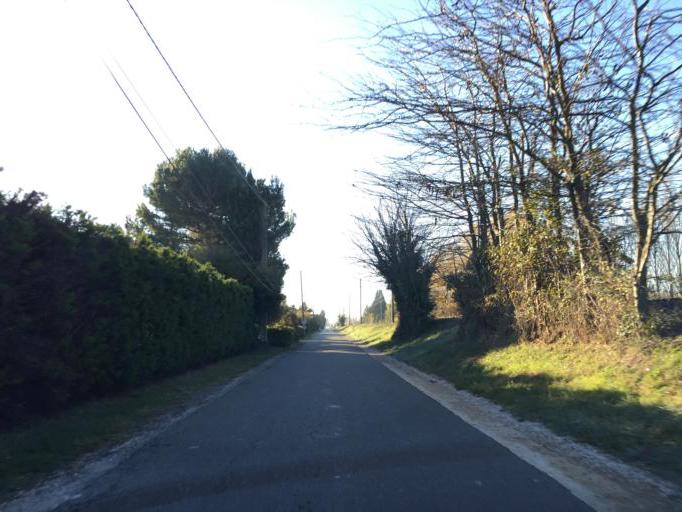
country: FR
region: Provence-Alpes-Cote d'Azur
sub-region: Departement du Vaucluse
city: Courthezon
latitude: 44.0815
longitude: 4.8898
